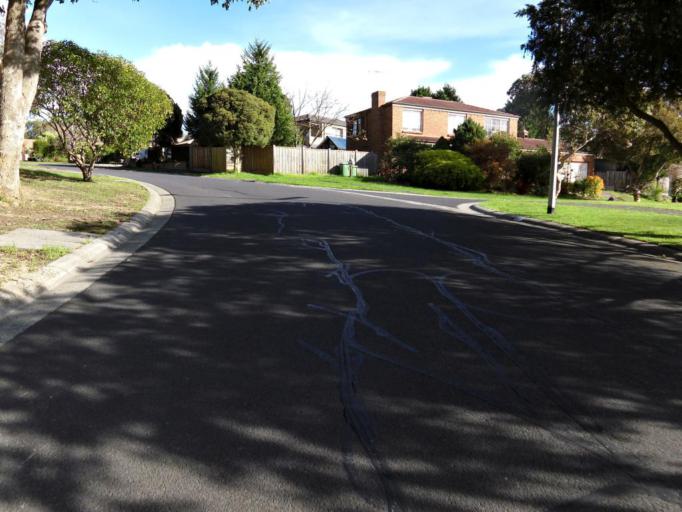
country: AU
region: Victoria
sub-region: Maroondah
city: Croydon Hills
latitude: -37.7708
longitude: 145.2639
